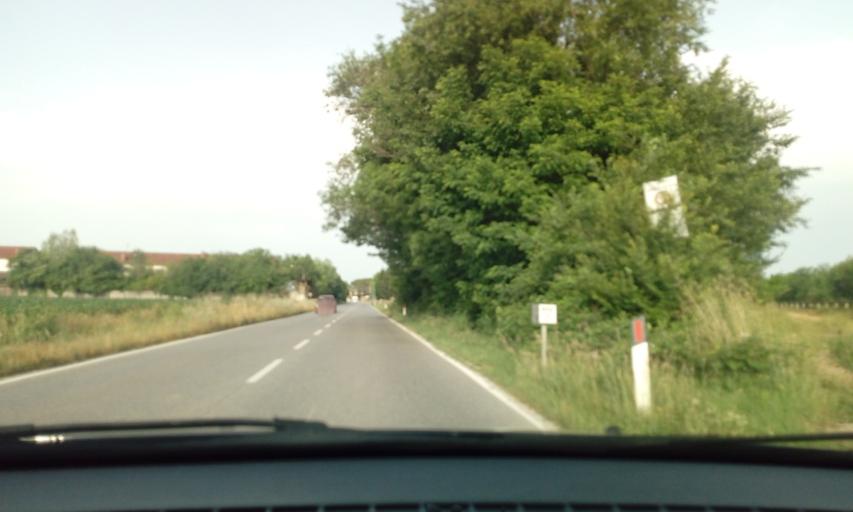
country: IT
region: Friuli Venezia Giulia
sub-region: Provincia di Udine
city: Ialmicco
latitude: 45.9165
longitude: 13.3565
